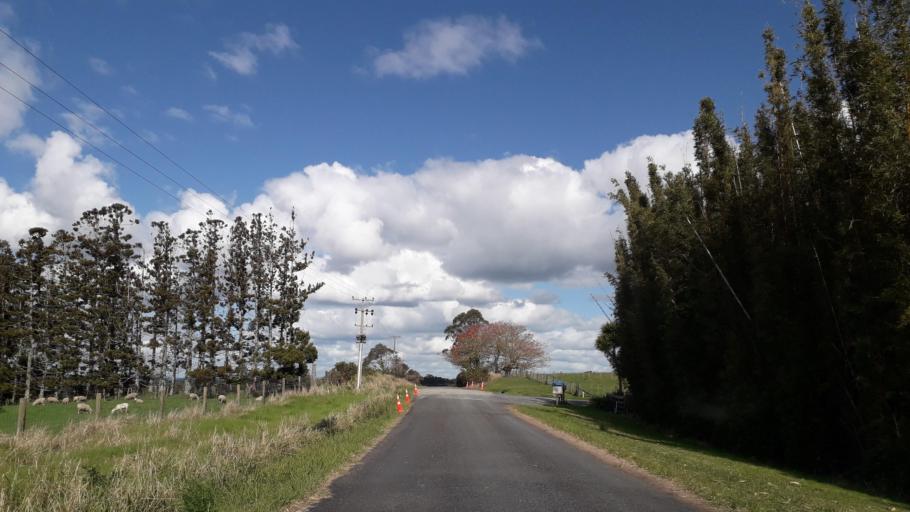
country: NZ
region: Northland
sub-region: Far North District
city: Kerikeri
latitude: -35.1815
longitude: 173.9349
